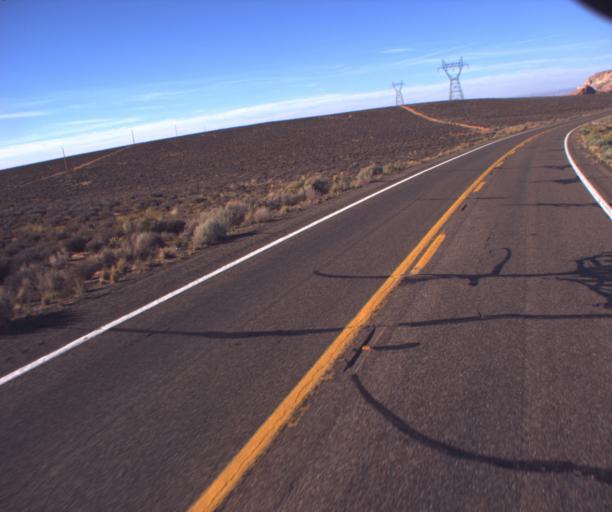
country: US
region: Arizona
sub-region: Coconino County
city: LeChee
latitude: 36.8067
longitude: -111.3063
